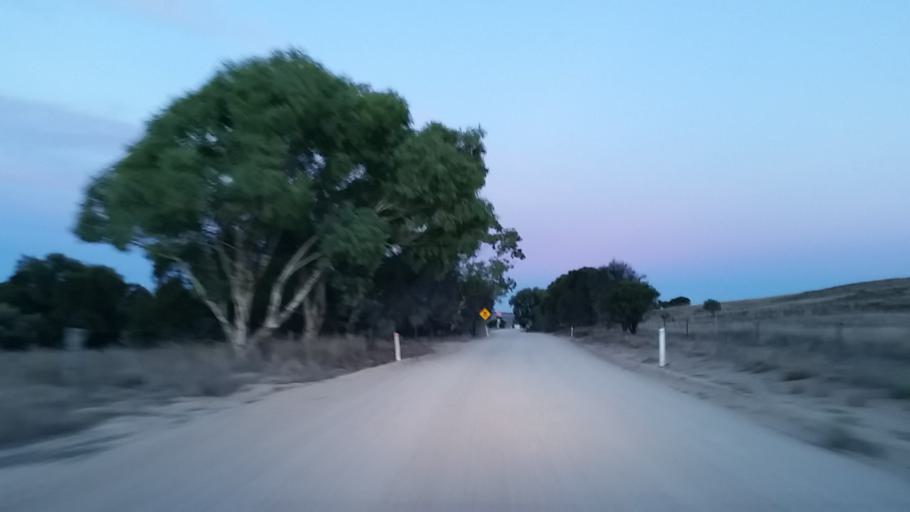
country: AU
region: South Australia
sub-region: Mount Barker
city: Callington
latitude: -35.1053
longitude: 139.0086
